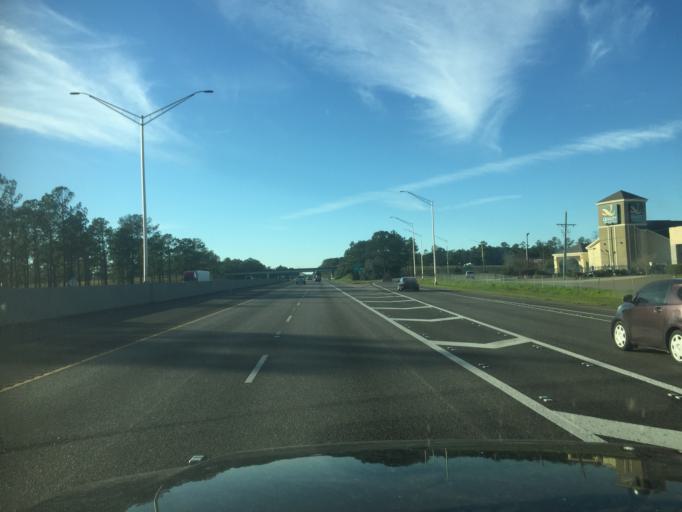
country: US
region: Louisiana
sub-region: Saint Tammany Parish
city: Slidell
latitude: 30.3120
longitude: -89.8220
